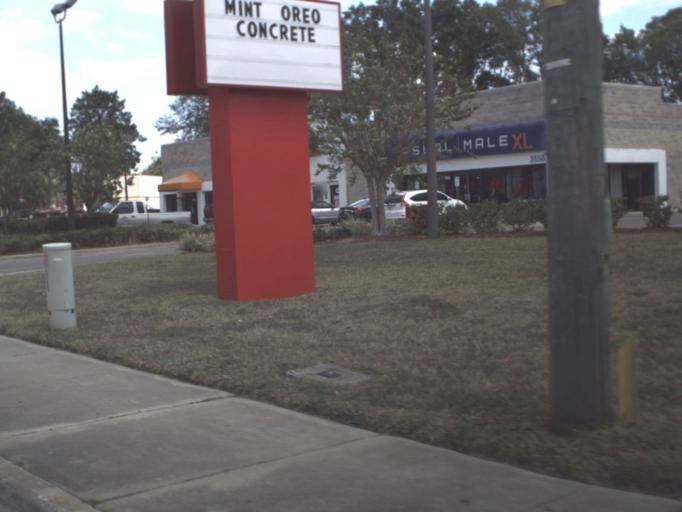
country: US
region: Florida
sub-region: Marion County
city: Ocala
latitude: 29.1530
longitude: -82.1823
